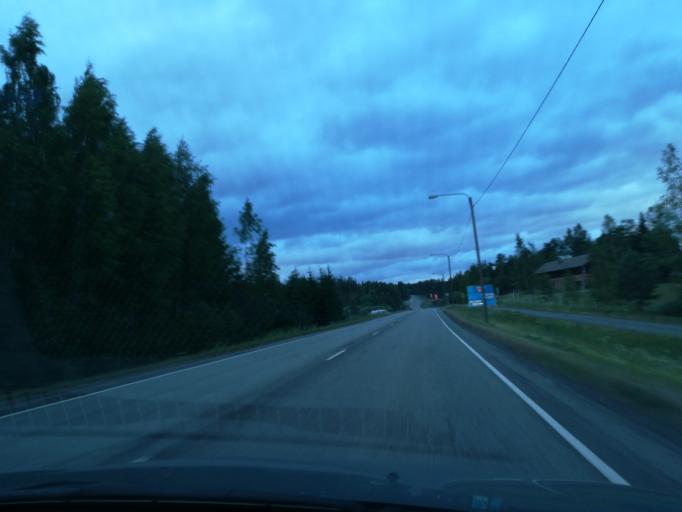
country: FI
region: Southern Savonia
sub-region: Mikkeli
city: Ristiina
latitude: 61.5080
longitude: 27.2388
